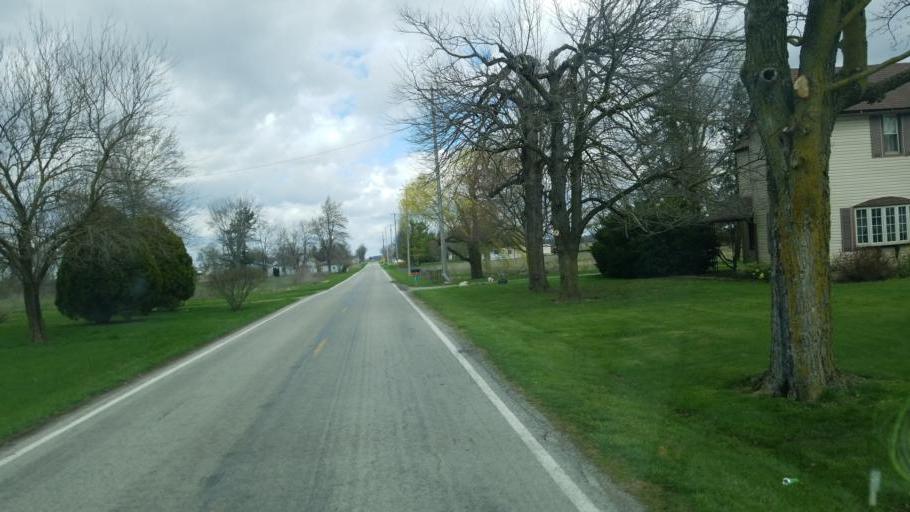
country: US
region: Ohio
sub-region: Union County
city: Richwood
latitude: 40.4204
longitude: -83.3105
